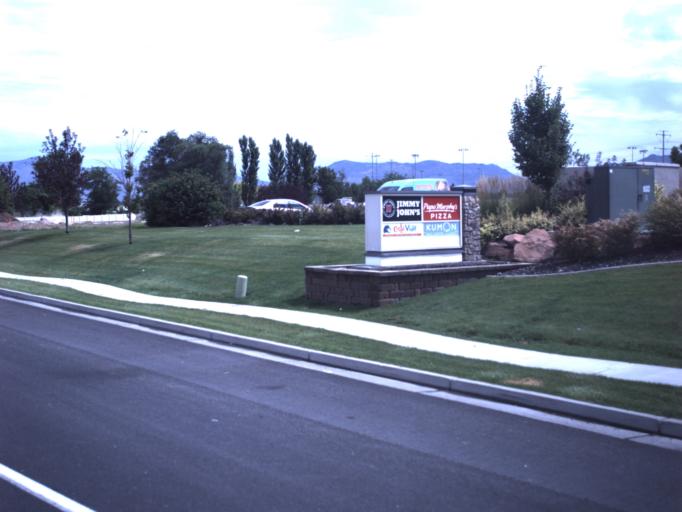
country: US
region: Utah
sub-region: Davis County
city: Clinton
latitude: 41.1421
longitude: -112.0644
